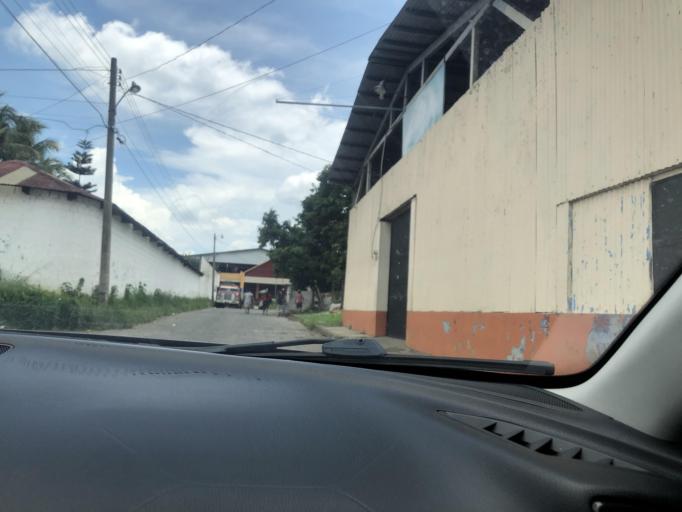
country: GT
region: Quetzaltenango
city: Coatepeque
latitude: 14.7084
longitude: -91.8660
